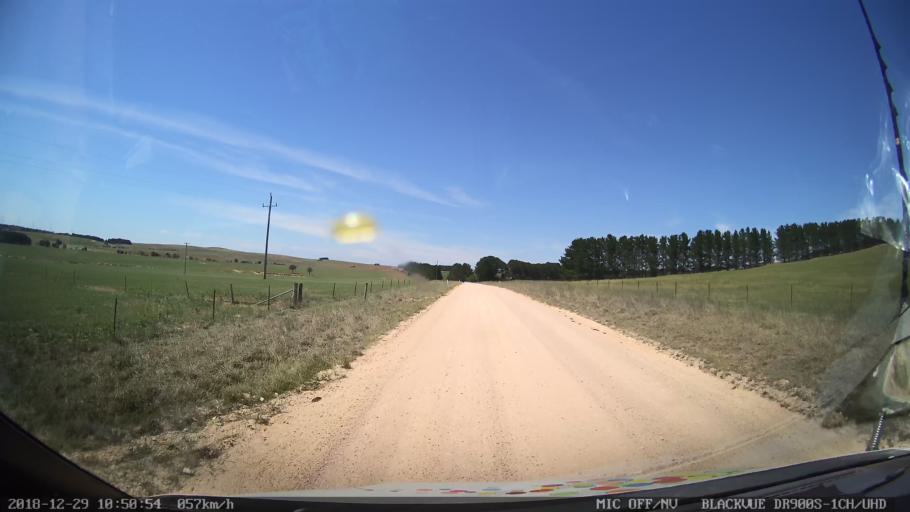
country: AU
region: New South Wales
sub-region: Palerang
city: Bungendore
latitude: -35.0851
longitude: 149.5240
